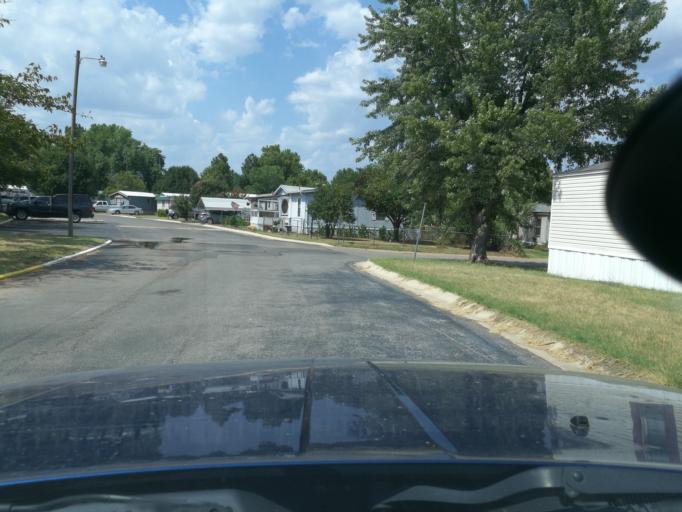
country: US
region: Oklahoma
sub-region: Oklahoma County
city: Del City
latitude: 35.4169
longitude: -97.4715
